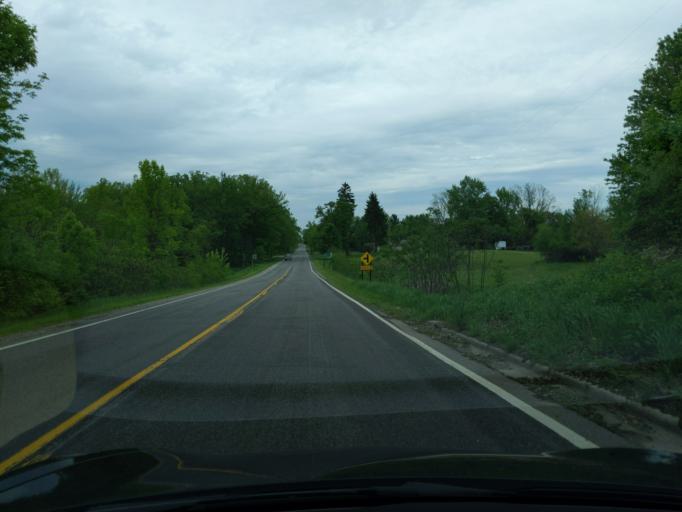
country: US
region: Michigan
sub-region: Ingham County
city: Leslie
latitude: 42.5216
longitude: -84.3562
